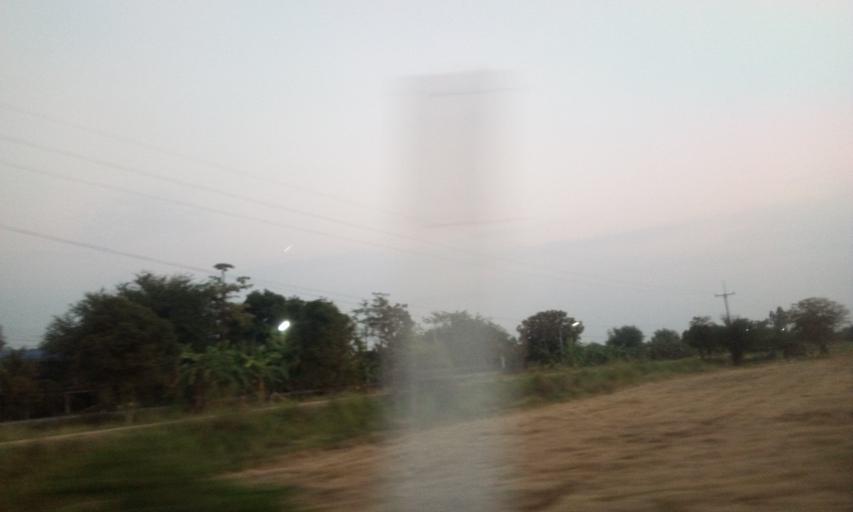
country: TH
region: Sing Buri
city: Phrom Buri
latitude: 14.8236
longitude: 100.4071
